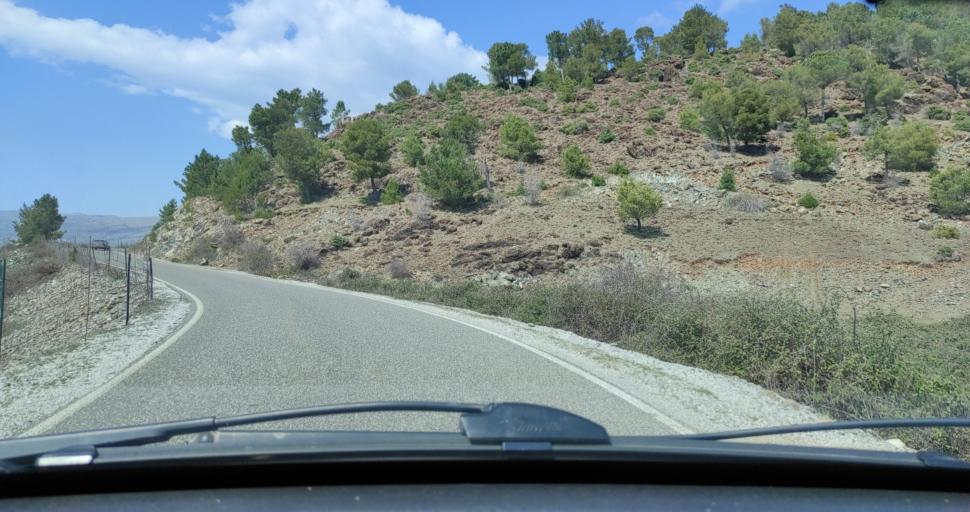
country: AL
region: Shkoder
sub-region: Rrethi i Shkodres
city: Vau i Dejes
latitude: 41.9890
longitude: 19.6455
